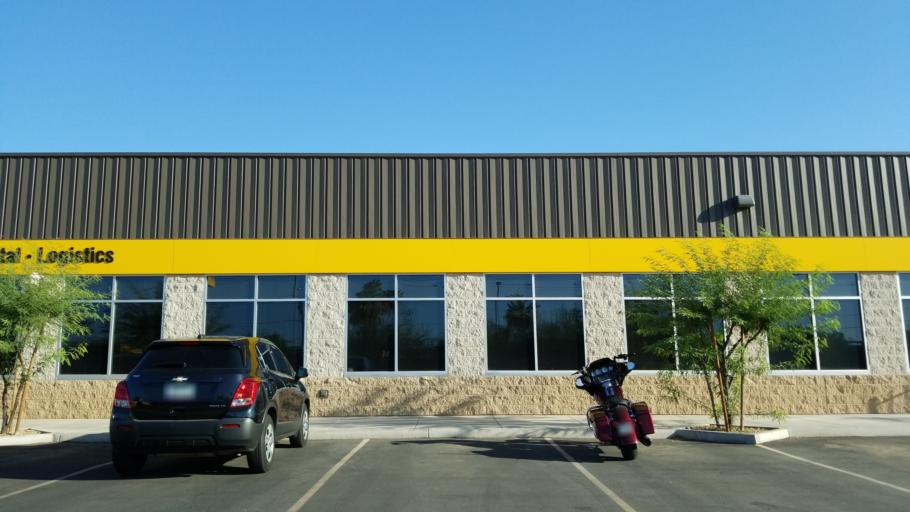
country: US
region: Arizona
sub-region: Maricopa County
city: Phoenix
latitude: 33.4277
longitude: -112.1012
